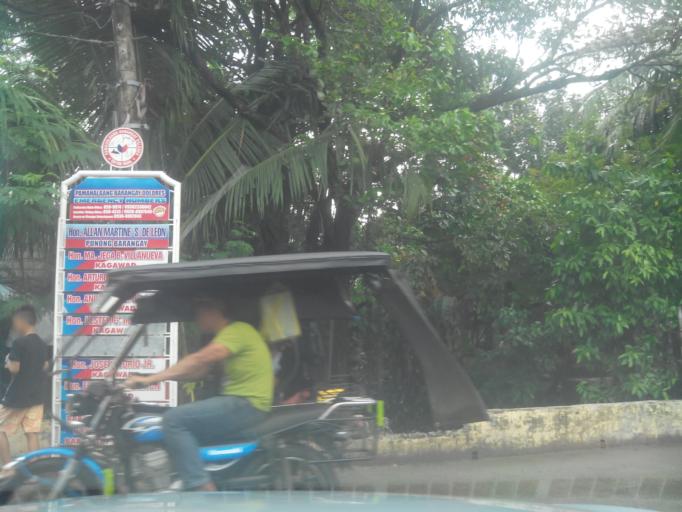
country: PH
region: Calabarzon
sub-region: Province of Rizal
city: Taytay
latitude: 14.5664
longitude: 121.1348
